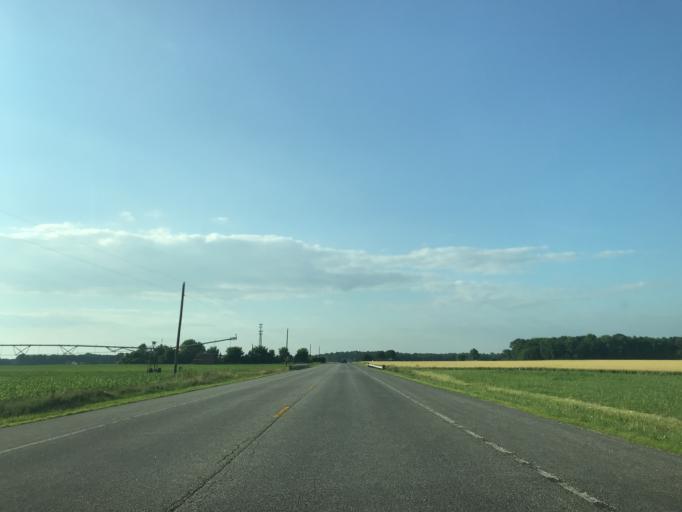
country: US
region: Maryland
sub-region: Caroline County
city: Denton
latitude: 38.8282
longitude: -75.7779
